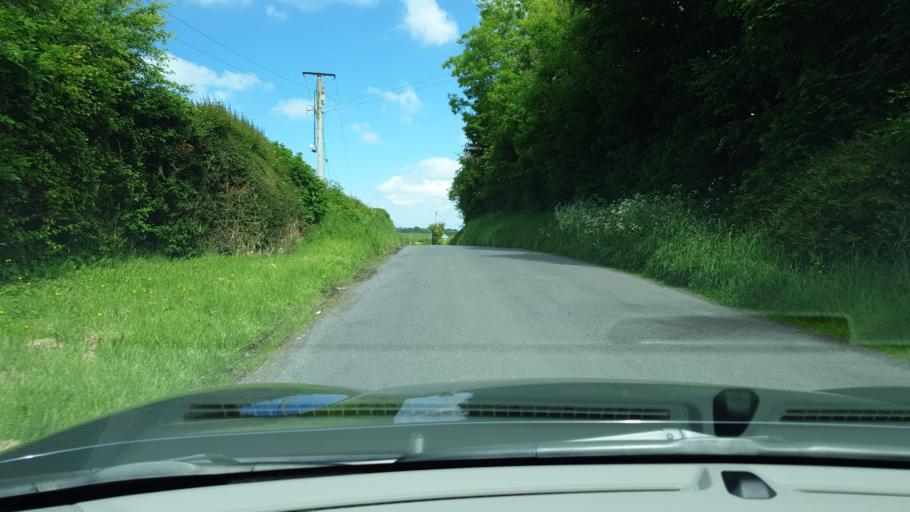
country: IE
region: Ulster
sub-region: An Cabhan
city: Kingscourt
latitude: 53.8074
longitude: -6.7356
